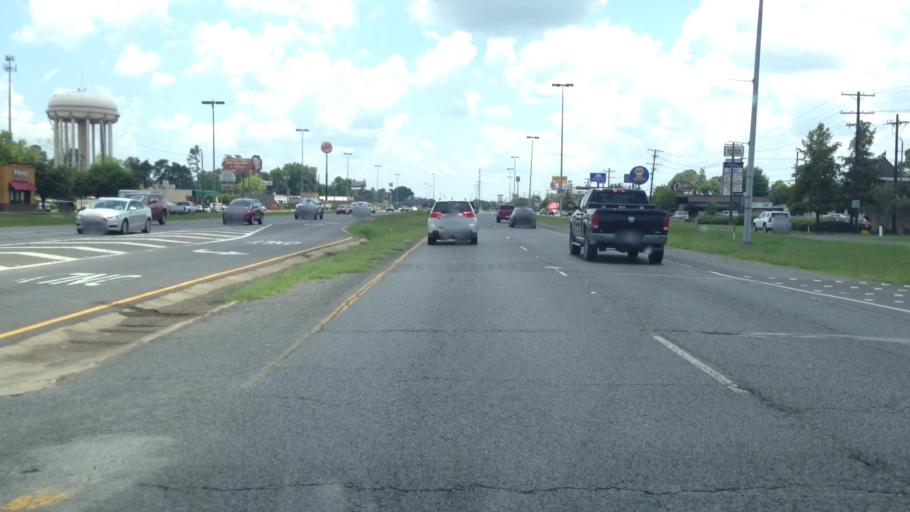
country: US
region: Louisiana
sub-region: Rapides Parish
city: Alexandria
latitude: 31.2929
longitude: -92.4777
